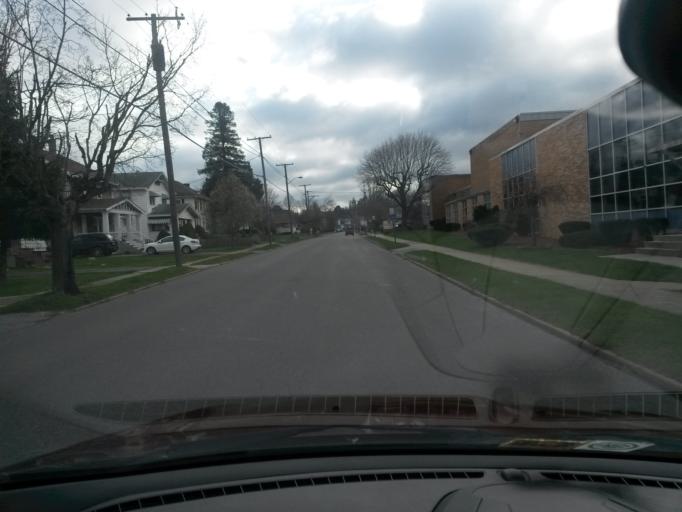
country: US
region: West Virginia
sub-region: Mercer County
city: Bluefield
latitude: 37.2527
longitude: -81.2260
